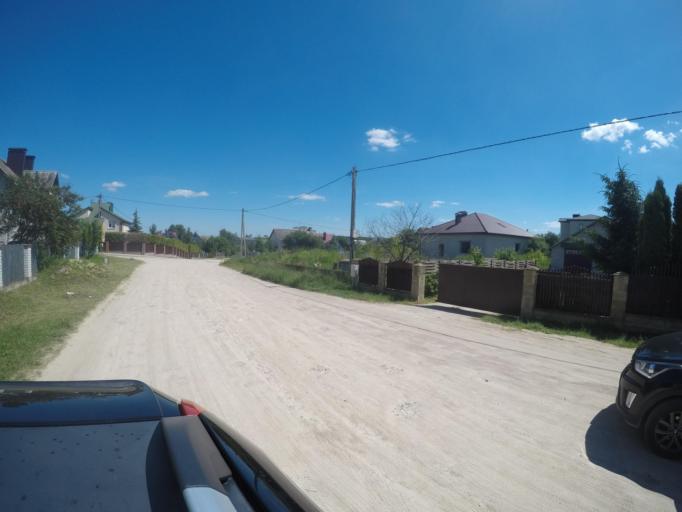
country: BY
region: Grodnenskaya
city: Hrodna
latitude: 53.7215
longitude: 23.8516
